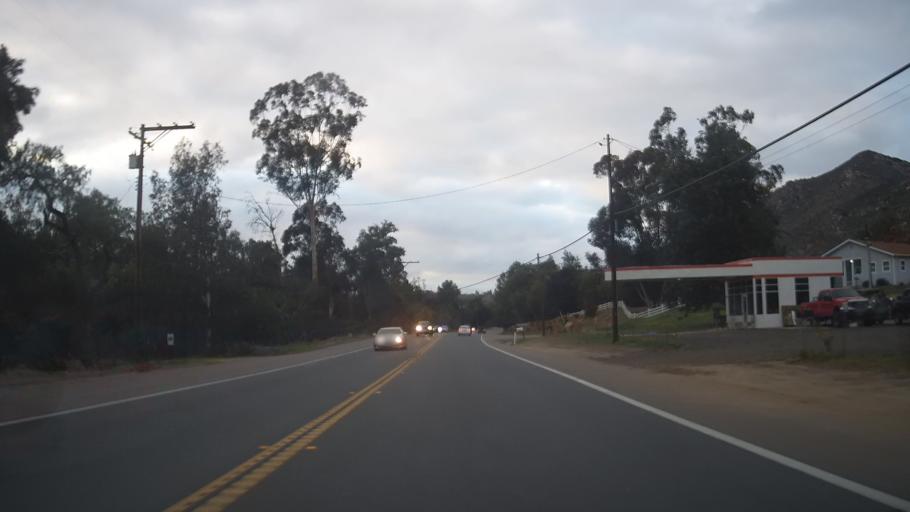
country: US
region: California
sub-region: San Diego County
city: Crest
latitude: 32.7799
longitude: -116.8712
